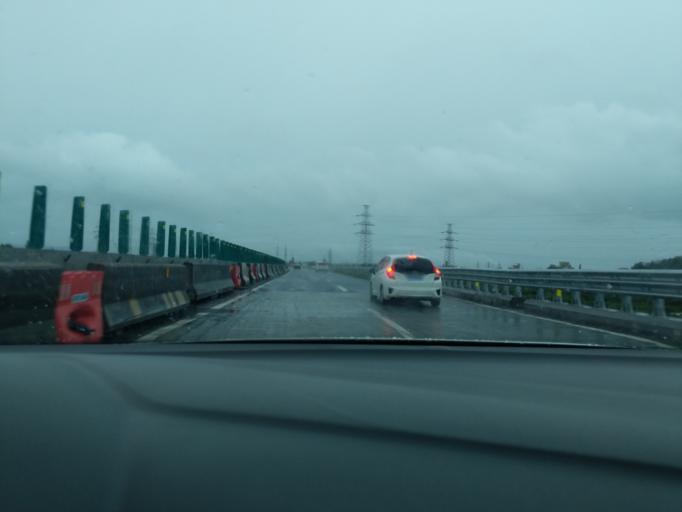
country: CN
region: Guangdong
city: Shuikou
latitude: 22.4649
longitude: 112.7480
